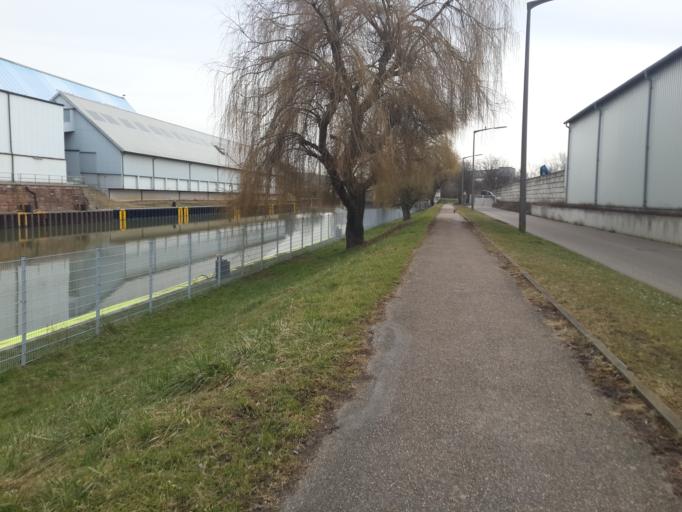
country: DE
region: Baden-Wuerttemberg
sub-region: Regierungsbezirk Stuttgart
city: Heilbronn
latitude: 49.1652
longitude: 9.2101
